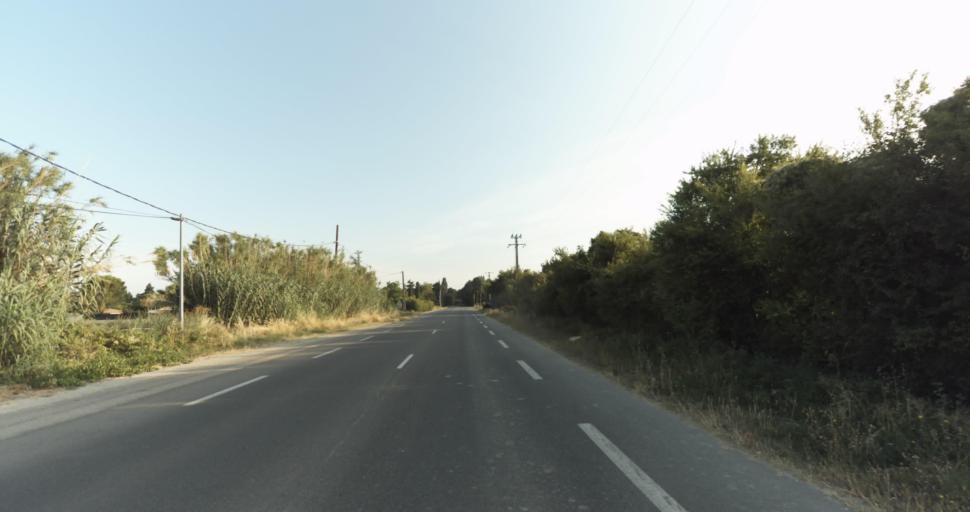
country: FR
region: Provence-Alpes-Cote d'Azur
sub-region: Departement du Vaucluse
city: Monteux
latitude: 44.0055
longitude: 5.0120
